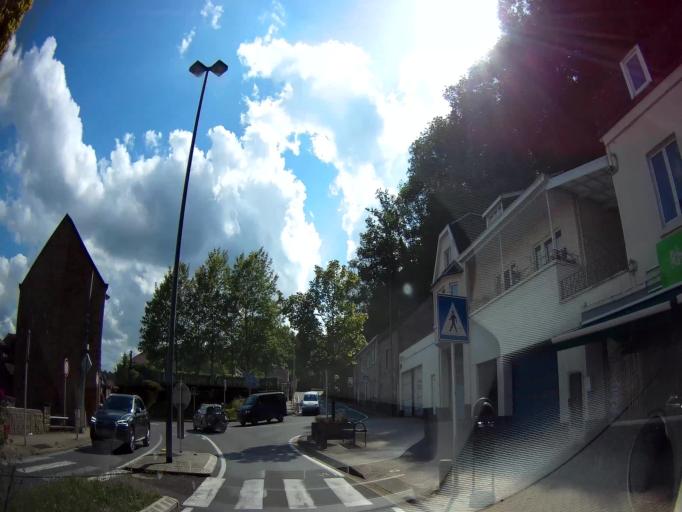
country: BE
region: Wallonia
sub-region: Province de Namur
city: Profondeville
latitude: 50.3485
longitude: 4.8515
